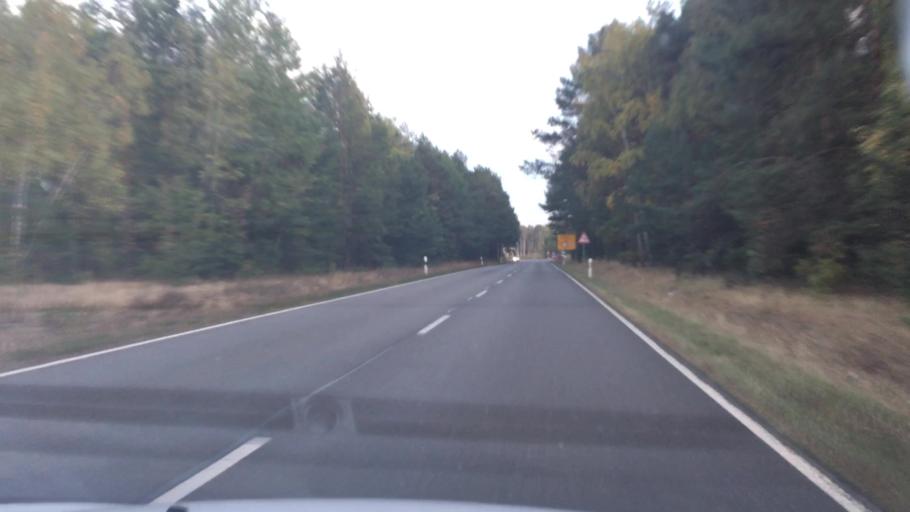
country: DE
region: Brandenburg
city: Welzow
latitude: 51.5665
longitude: 14.1077
